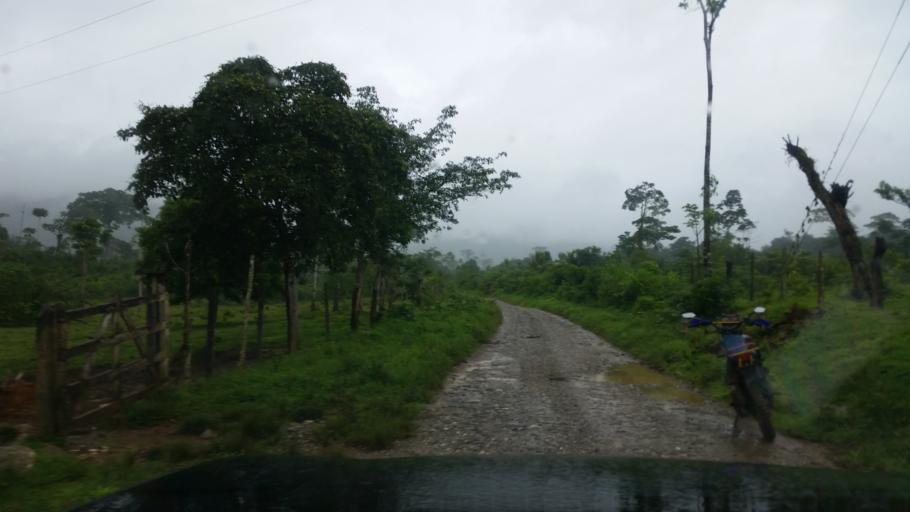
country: NI
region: Atlantico Norte (RAAN)
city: Bonanza
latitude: 14.0844
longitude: -84.6773
